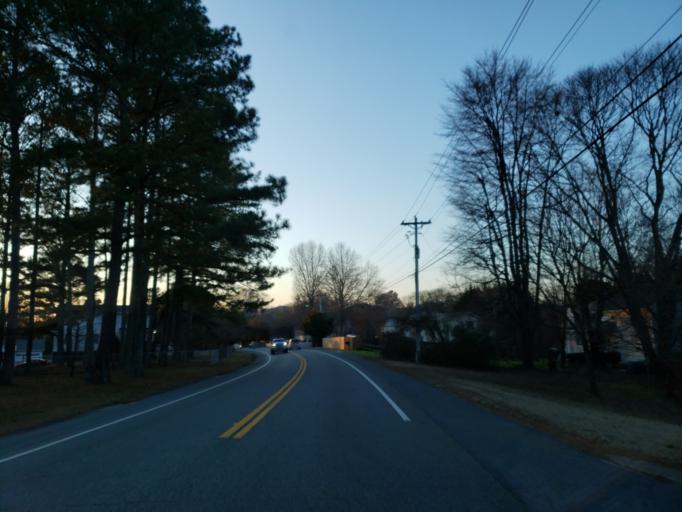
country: US
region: Georgia
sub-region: Cherokee County
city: Woodstock
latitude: 34.1169
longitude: -84.4632
